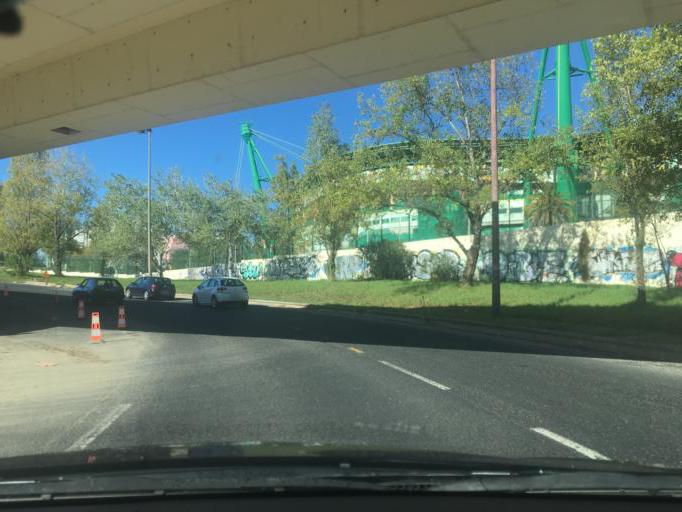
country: PT
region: Lisbon
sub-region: Odivelas
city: Olival do Basto
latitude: 38.7595
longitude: -9.1592
